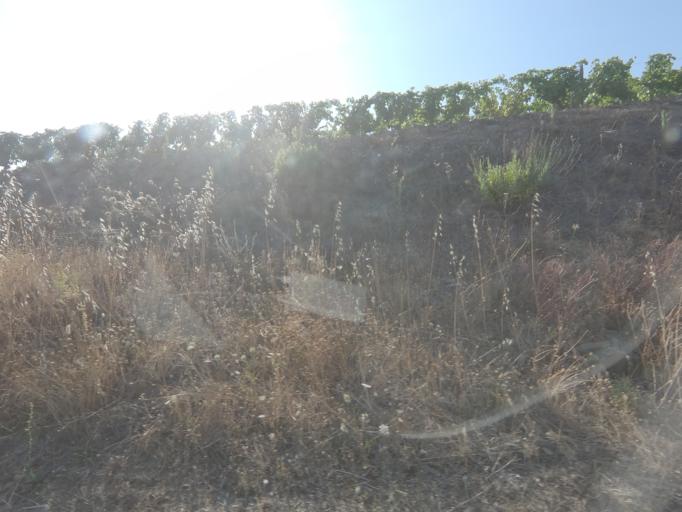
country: PT
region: Viseu
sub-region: Tabuaco
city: Tabuaco
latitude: 41.1860
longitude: -7.5309
